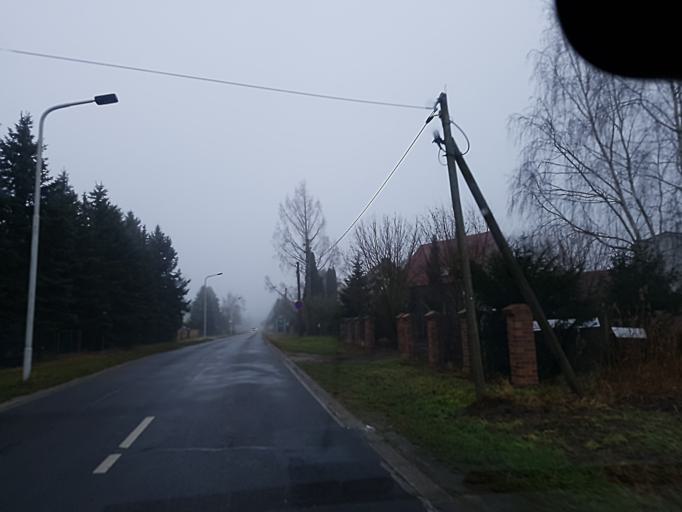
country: DE
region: Brandenburg
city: Finsterwalde
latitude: 51.6455
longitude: 13.7102
